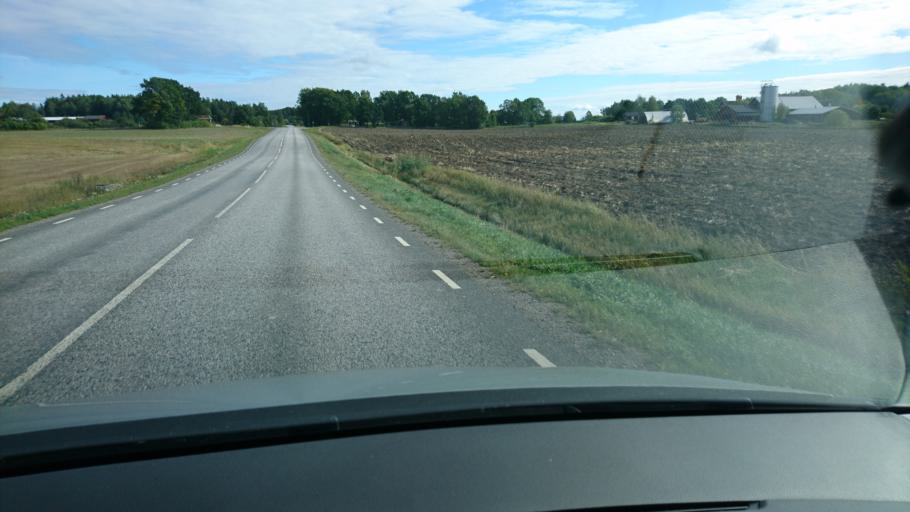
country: SE
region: Soedermanland
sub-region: Strangnas Kommun
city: Stallarholmen
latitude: 59.3485
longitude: 17.1634
